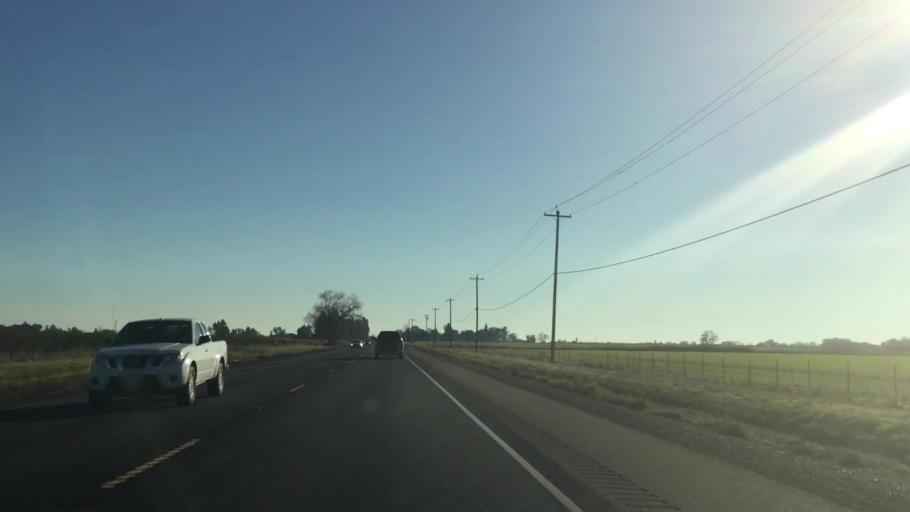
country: US
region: California
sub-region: Butte County
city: Palermo
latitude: 39.4175
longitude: -121.6062
